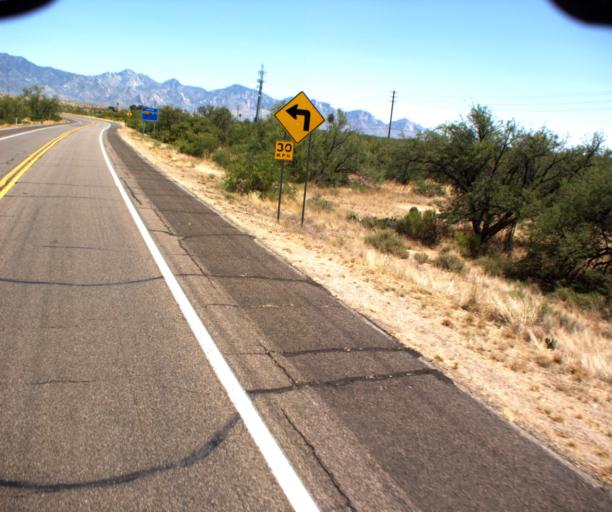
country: US
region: Arizona
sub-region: Pima County
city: Catalina
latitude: 32.5595
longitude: -110.9361
